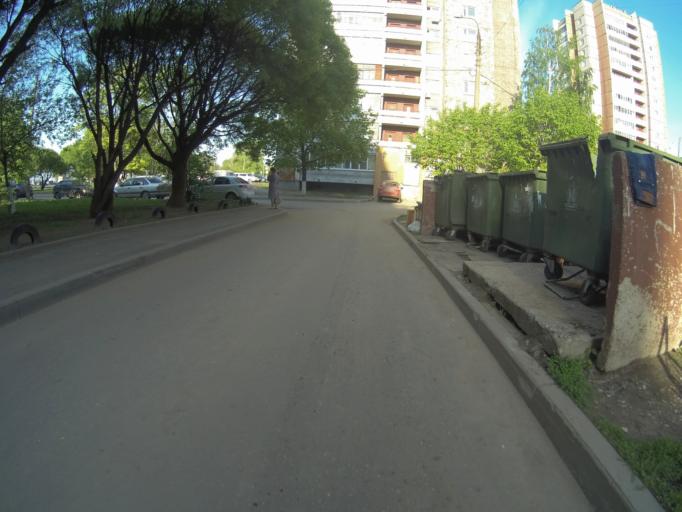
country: RU
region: Vladimir
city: Kommunar
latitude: 56.1727
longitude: 40.4567
